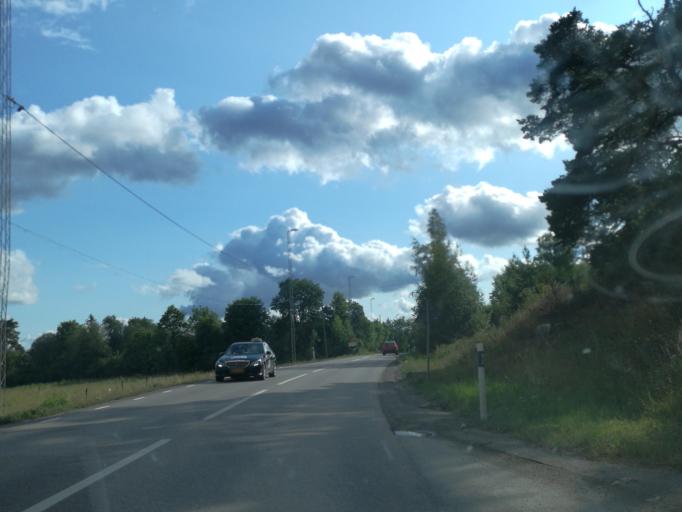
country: SE
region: Stockholm
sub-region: Upplands Vasby Kommun
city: Upplands Vaesby
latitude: 59.5258
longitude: 17.9642
